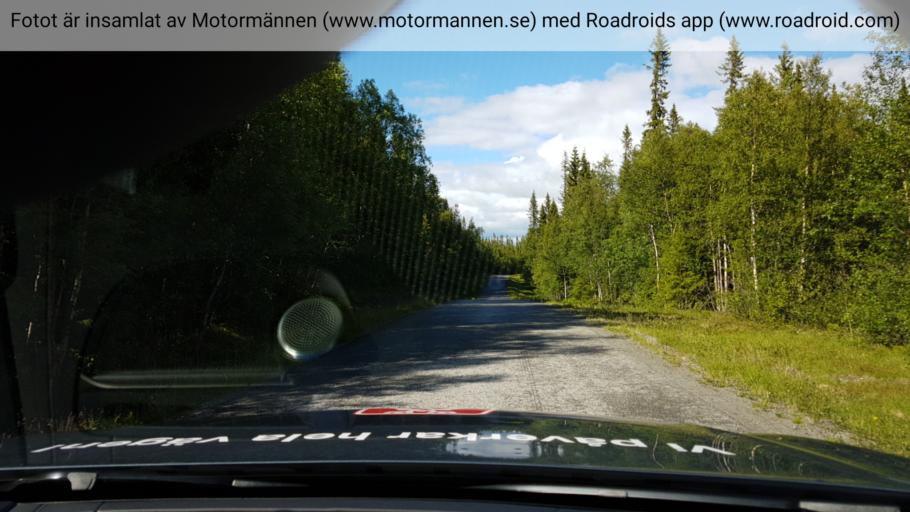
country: SE
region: Jaemtland
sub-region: Bergs Kommun
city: Hoverberg
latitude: 63.0131
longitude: 13.9423
